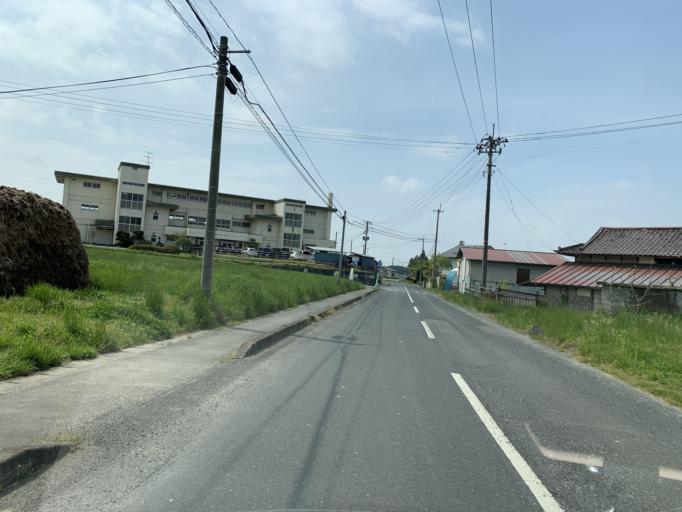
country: JP
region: Iwate
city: Ichinoseki
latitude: 38.8276
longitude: 141.2022
